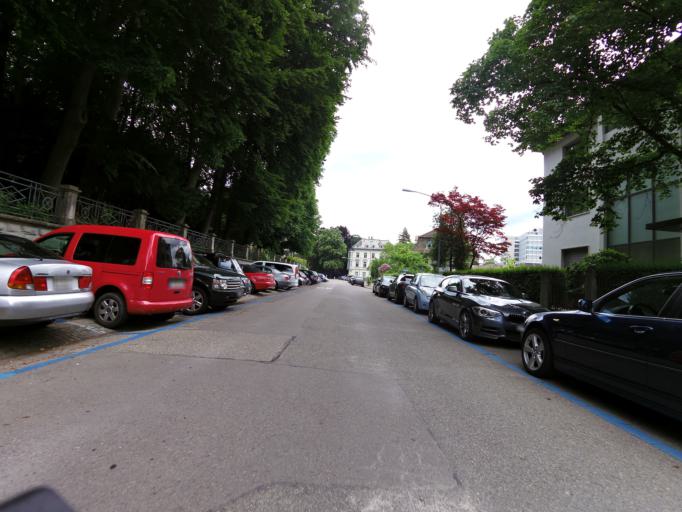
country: CH
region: Zurich
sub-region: Bezirk Zuerich
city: Zuerich (Kreis 2) / Enge
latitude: 47.3660
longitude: 8.5304
